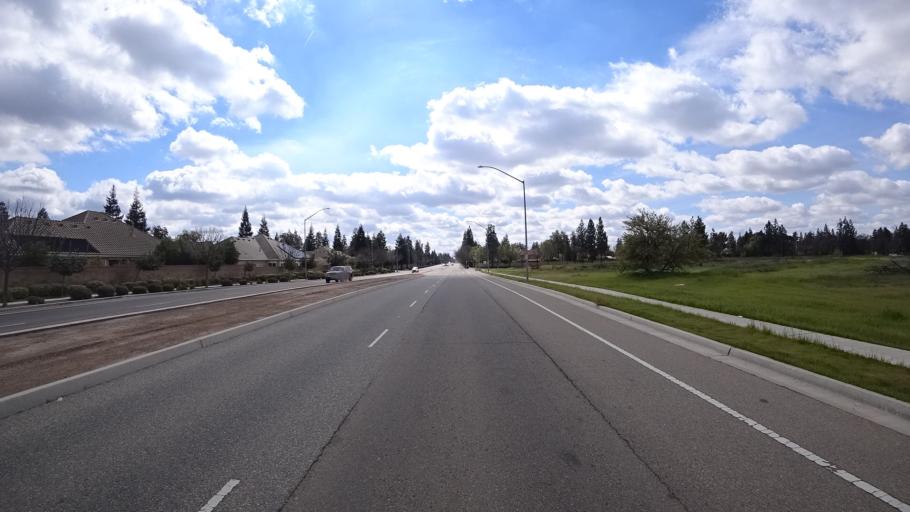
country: US
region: California
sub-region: Fresno County
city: West Park
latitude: 36.8349
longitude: -119.8626
